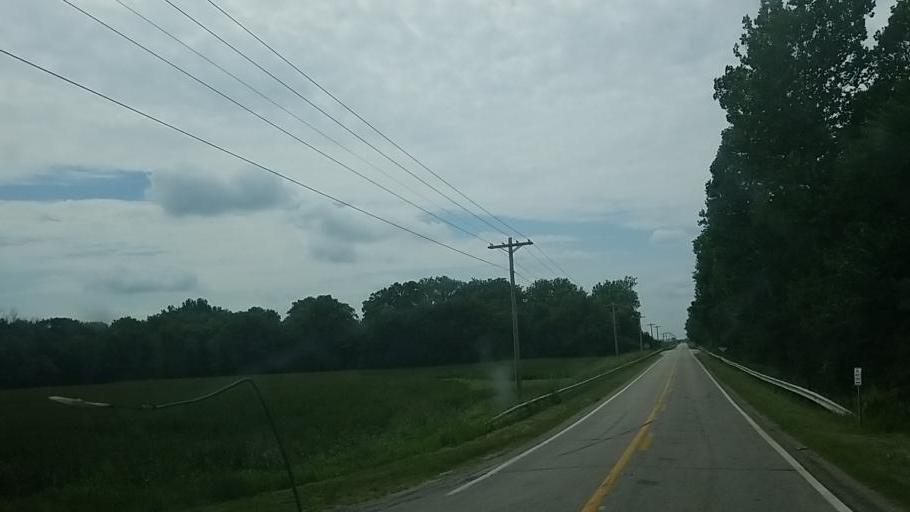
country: US
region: Ohio
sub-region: Franklin County
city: Groveport
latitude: 39.8279
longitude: -82.8887
